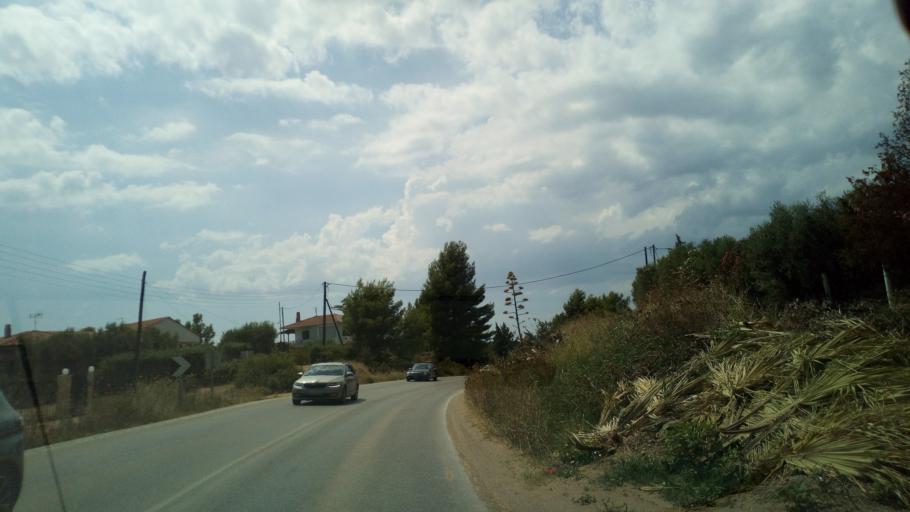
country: GR
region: Central Macedonia
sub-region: Nomos Chalkidikis
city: Nikiti
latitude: 40.2310
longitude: 23.6207
